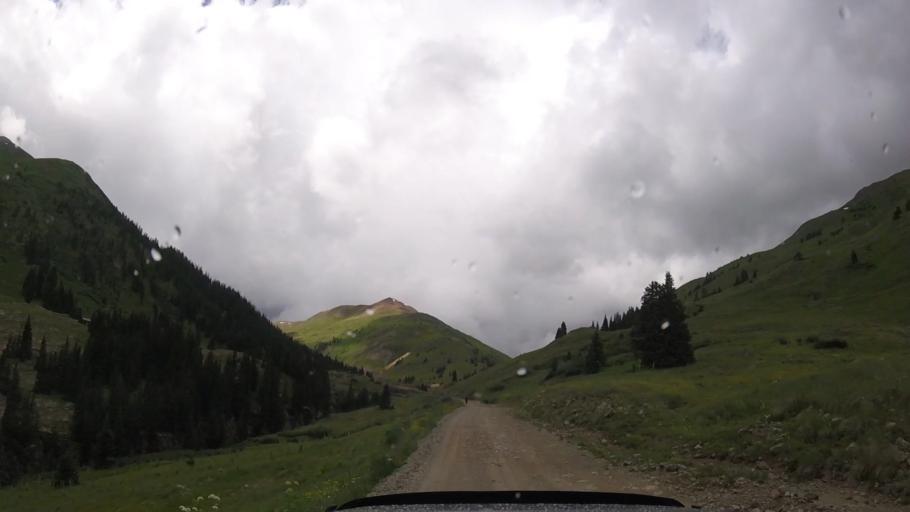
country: US
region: Colorado
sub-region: Ouray County
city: Ouray
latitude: 37.9275
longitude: -107.5644
